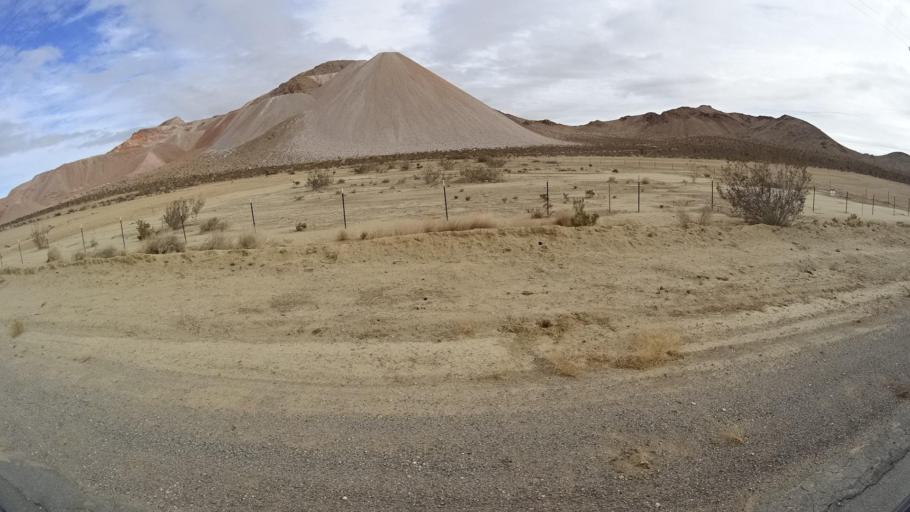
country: US
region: California
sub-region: Kern County
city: Mojave
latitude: 34.9790
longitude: -118.2099
